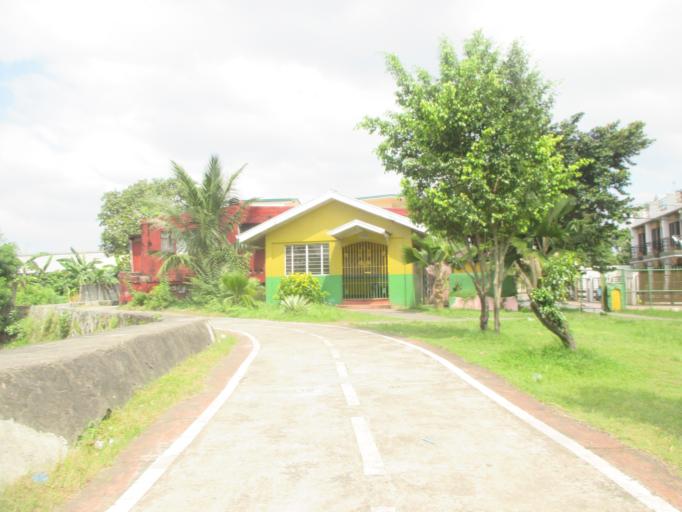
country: PH
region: Calabarzon
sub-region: Province of Rizal
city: Antipolo
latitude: 14.6428
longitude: 121.1071
